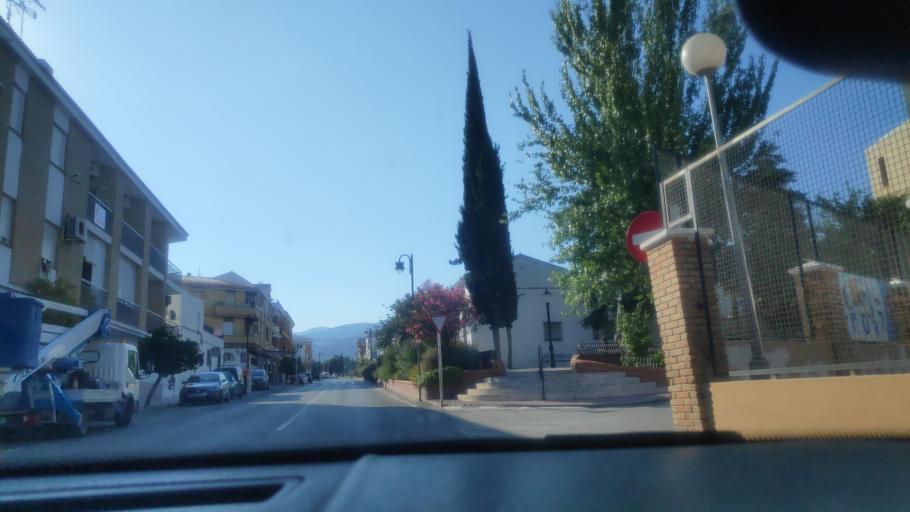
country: ES
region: Andalusia
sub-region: Provincia de Jaen
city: Mancha Real
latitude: 37.7865
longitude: -3.6068
